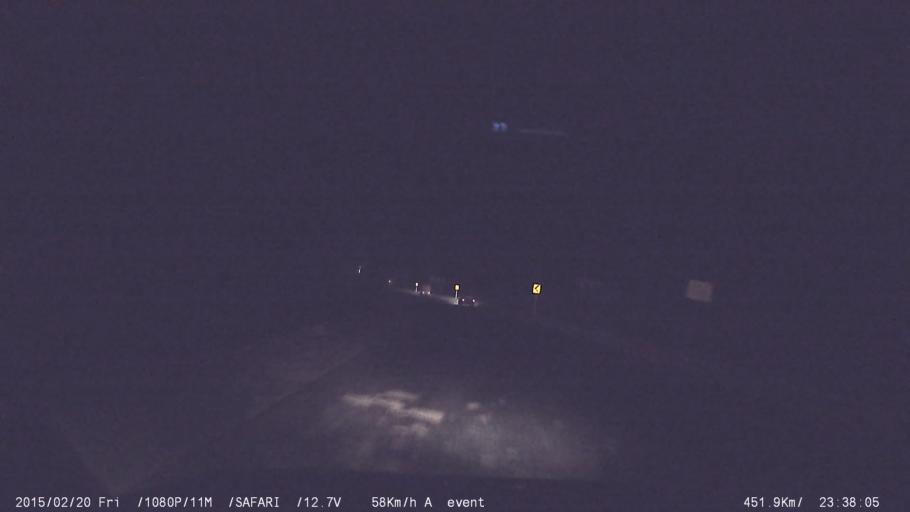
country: IN
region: Kerala
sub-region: Palakkad district
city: Palakkad
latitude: 10.7379
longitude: 76.6206
